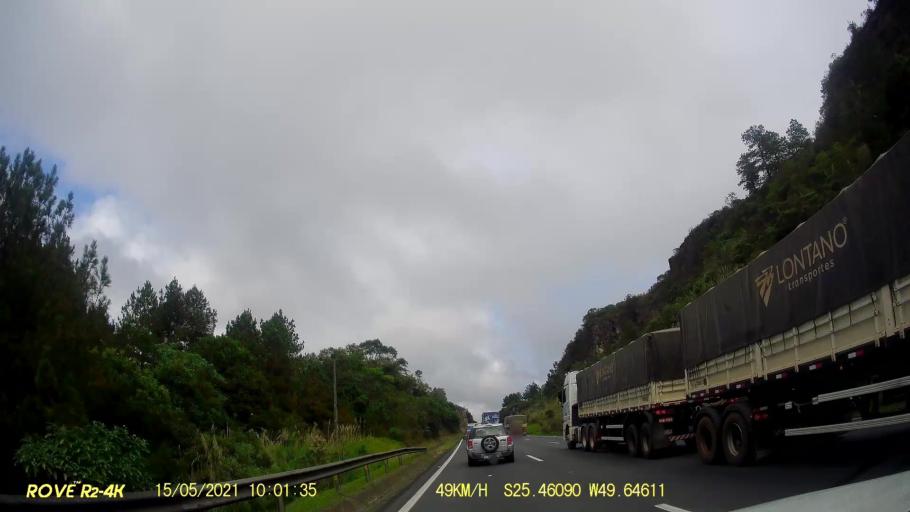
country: BR
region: Parana
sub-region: Campo Largo
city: Campo Largo
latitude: -25.4609
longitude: -49.6461
